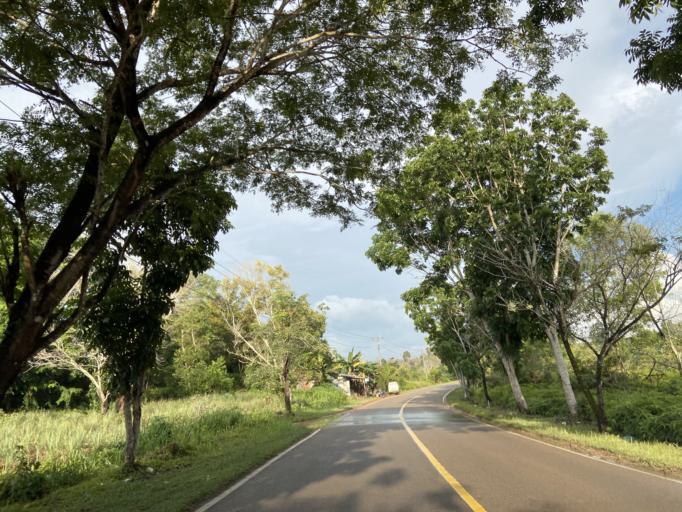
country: ID
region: Riau Islands
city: Tanjungpinang
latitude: 0.9453
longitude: 104.0624
